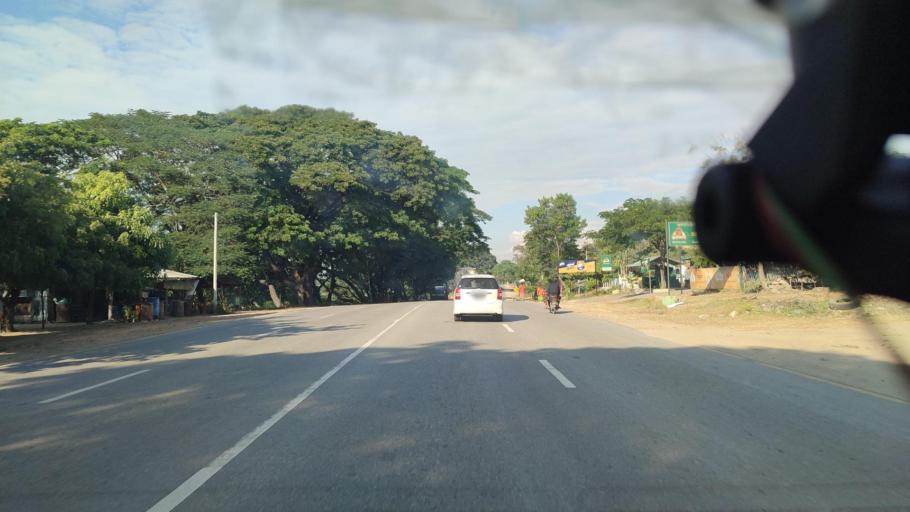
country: MM
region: Mandalay
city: Pyinmana
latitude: 20.0712
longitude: 96.2571
